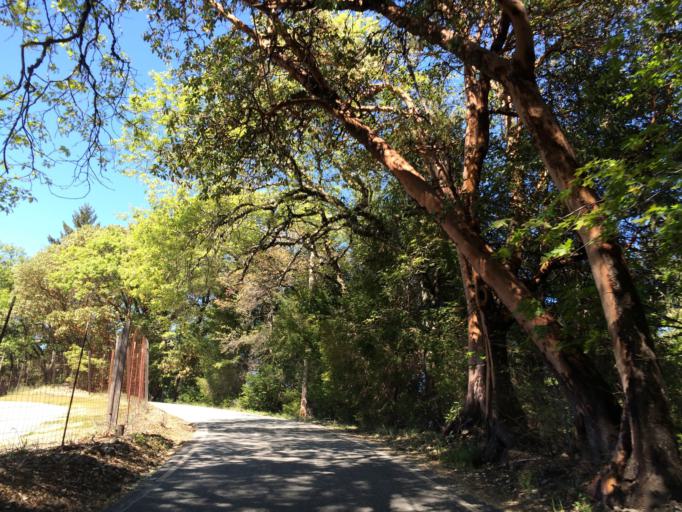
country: US
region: California
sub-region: Santa Clara County
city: Lexington Hills
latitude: 37.1783
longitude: -122.0272
